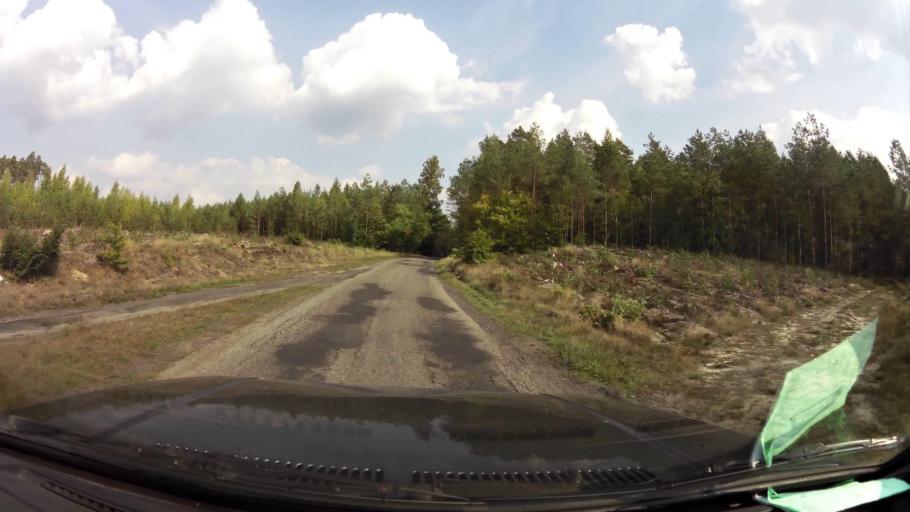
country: PL
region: West Pomeranian Voivodeship
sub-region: Powiat koszalinski
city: Bobolice
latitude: 54.0850
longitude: 16.4782
